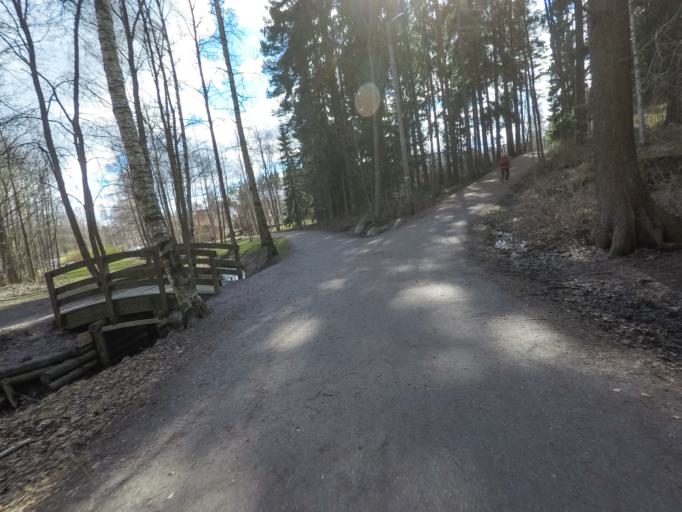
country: FI
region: Uusimaa
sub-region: Helsinki
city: Vantaa
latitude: 60.2217
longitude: 25.0479
